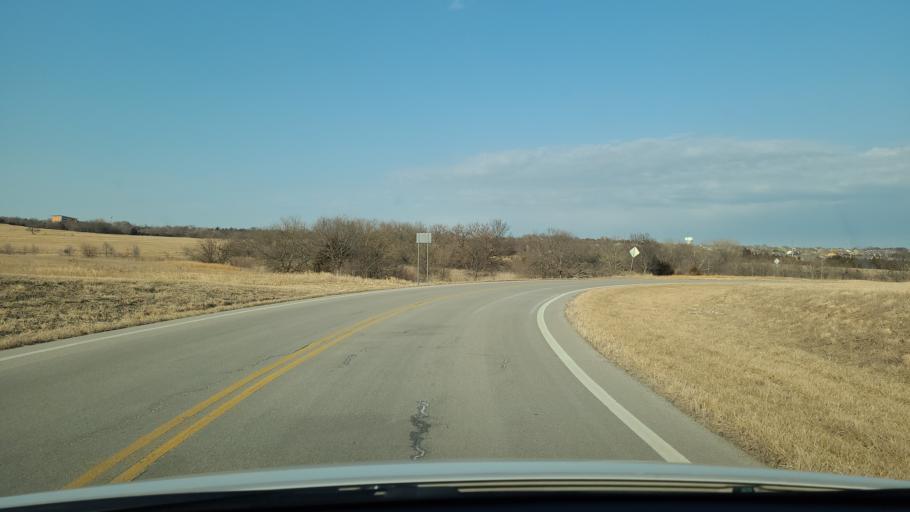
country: US
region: Kansas
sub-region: Douglas County
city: Lawrence
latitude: 38.9587
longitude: -95.3414
